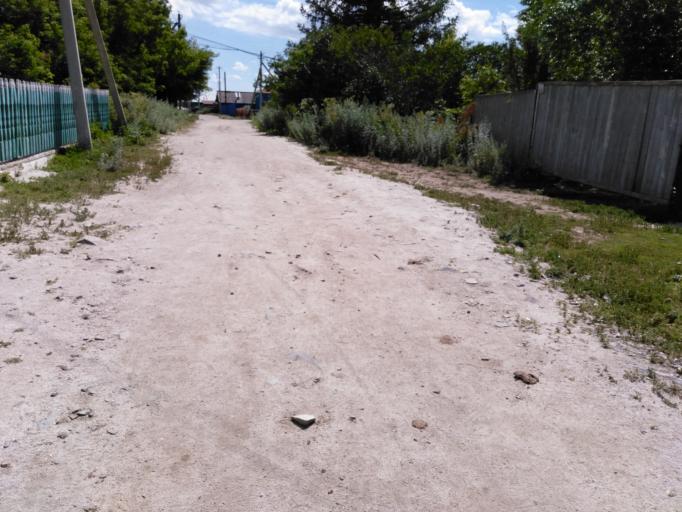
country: RU
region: Bashkortostan
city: Akhunovo
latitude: 54.2081
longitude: 59.5996
